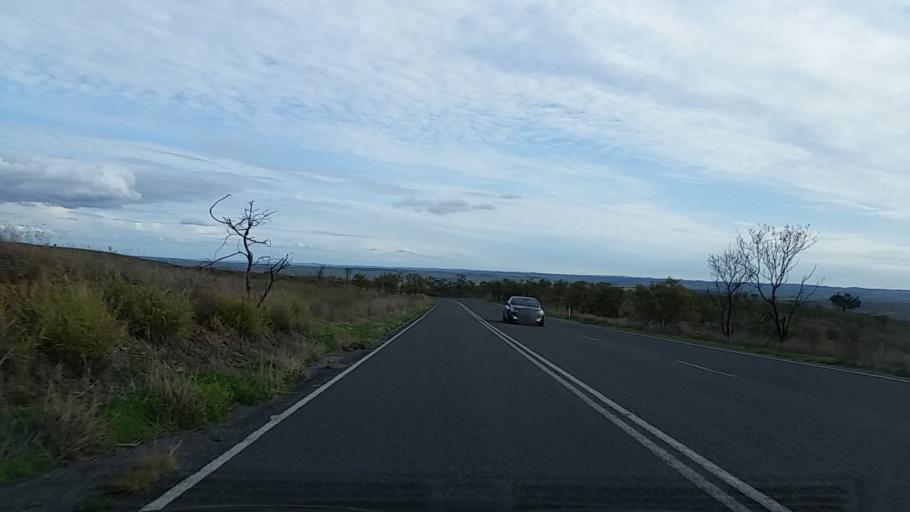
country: AU
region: South Australia
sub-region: Mount Barker
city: Callington
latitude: -35.1116
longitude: 139.0738
